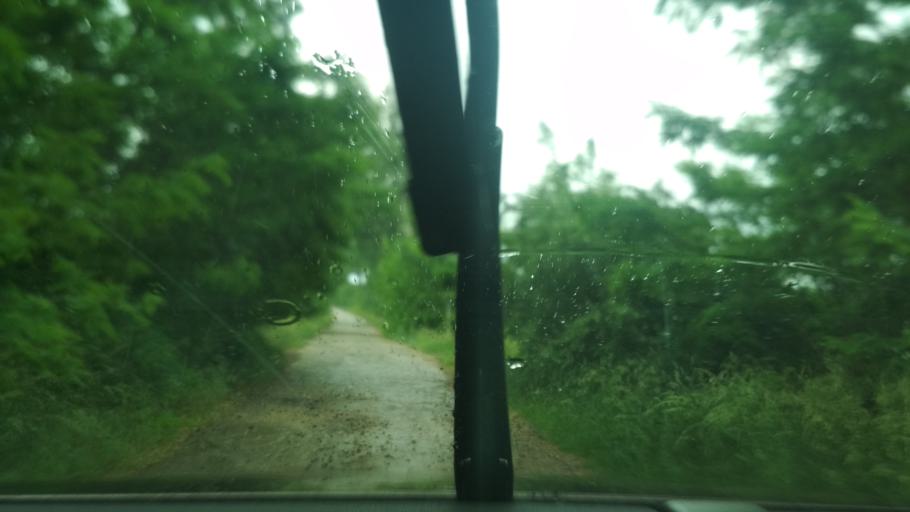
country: MD
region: Singerei
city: Biruinta
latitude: 47.7443
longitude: 28.1380
